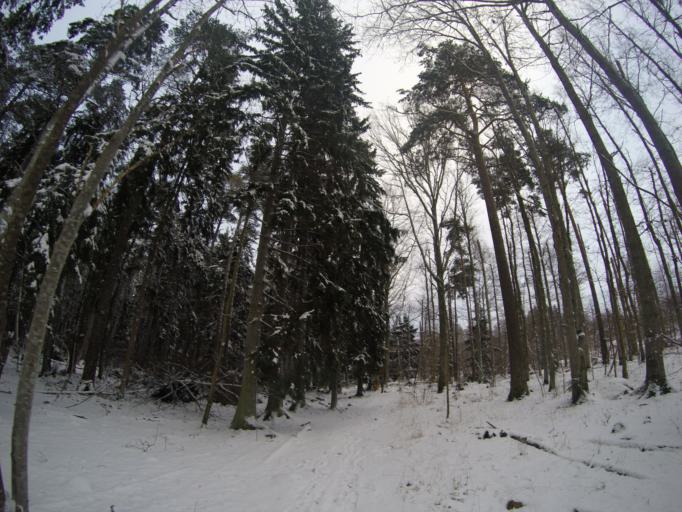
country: SE
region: OEstergoetland
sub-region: Linkopings Kommun
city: Malmslatt
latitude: 58.4126
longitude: 15.5312
